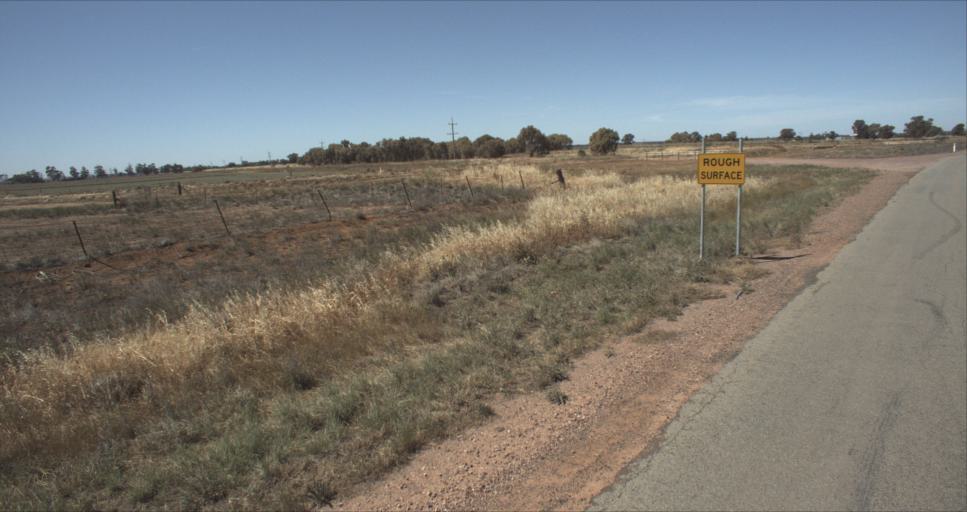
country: AU
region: New South Wales
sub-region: Leeton
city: Leeton
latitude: -34.5663
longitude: 146.3117
